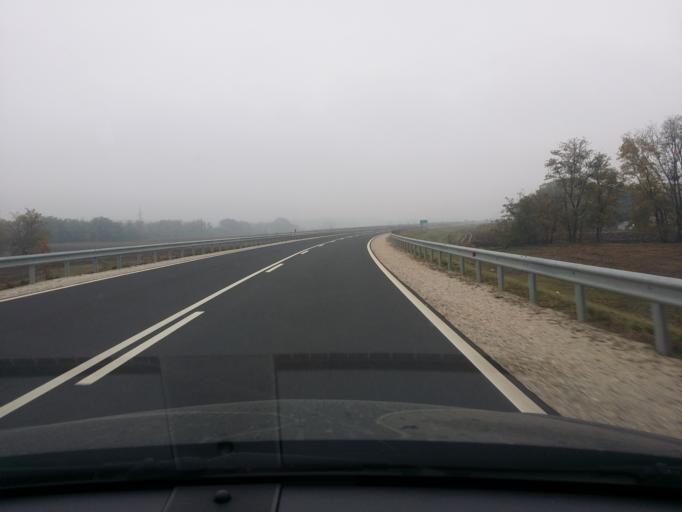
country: HU
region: Szabolcs-Szatmar-Bereg
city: Kalmanhaza
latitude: 47.9246
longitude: 21.6431
